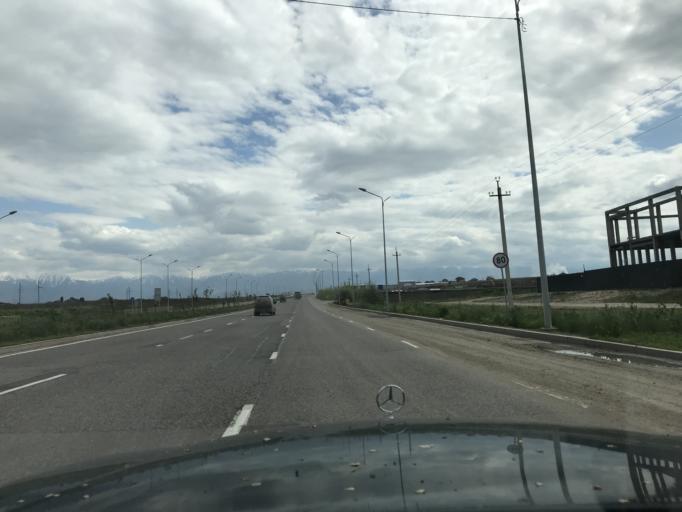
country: KZ
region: Almaty Oblysy
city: Burunday
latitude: 43.3478
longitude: 76.8337
